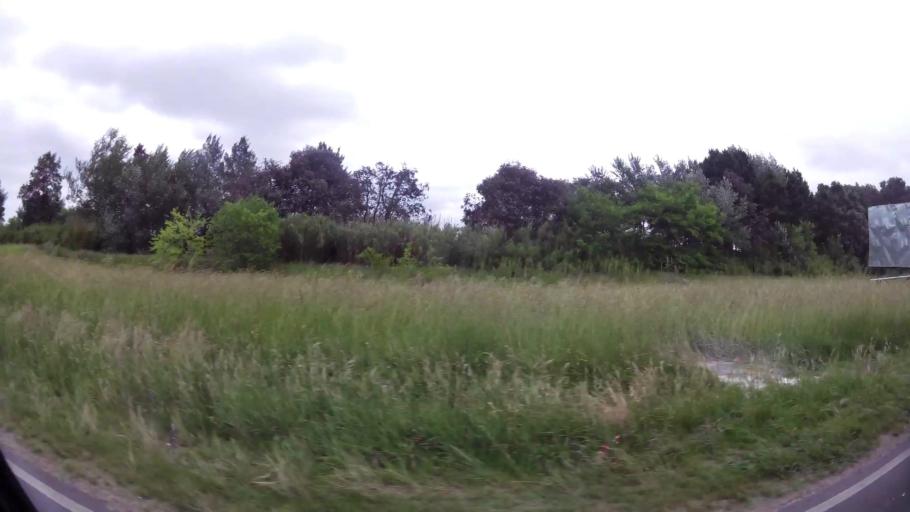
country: AR
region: Buenos Aires
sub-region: Partido de Ezeiza
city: Ezeiza
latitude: -34.9100
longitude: -58.5045
